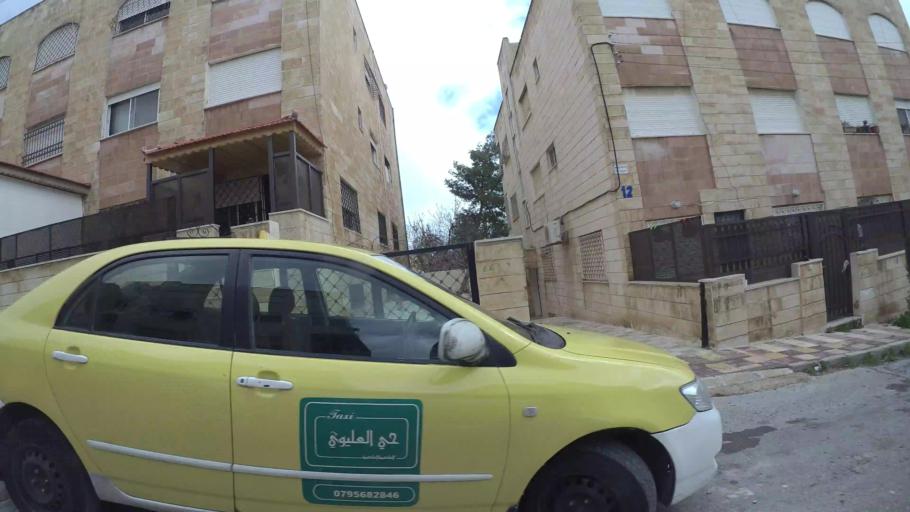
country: JO
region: Amman
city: Al Jubayhah
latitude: 32.0580
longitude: 35.8731
